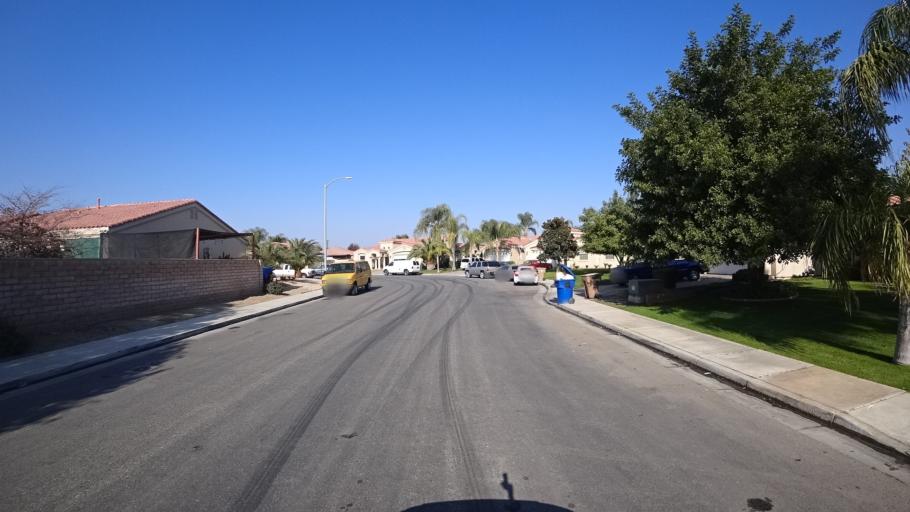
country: US
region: California
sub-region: Kern County
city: Greenfield
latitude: 35.2796
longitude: -119.0126
